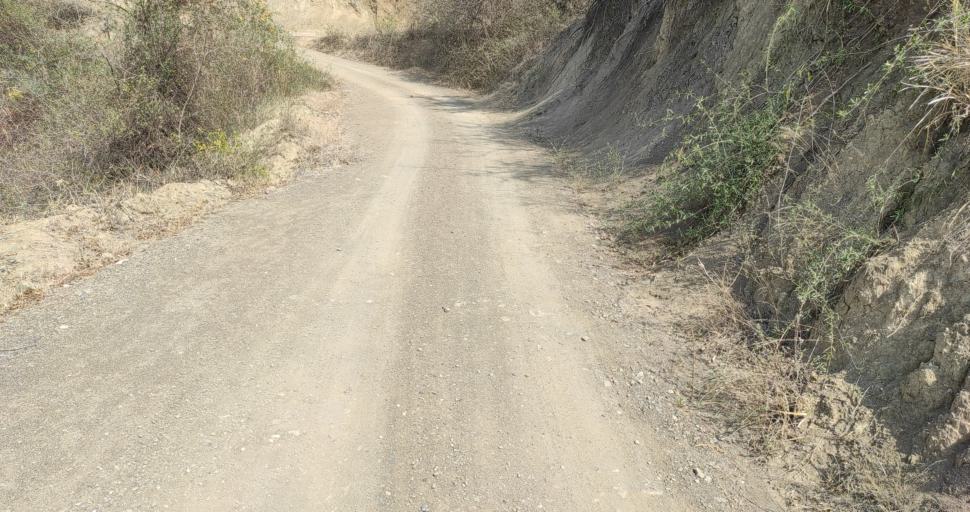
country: EC
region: Loja
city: Catacocha
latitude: -4.0072
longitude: -79.7101
